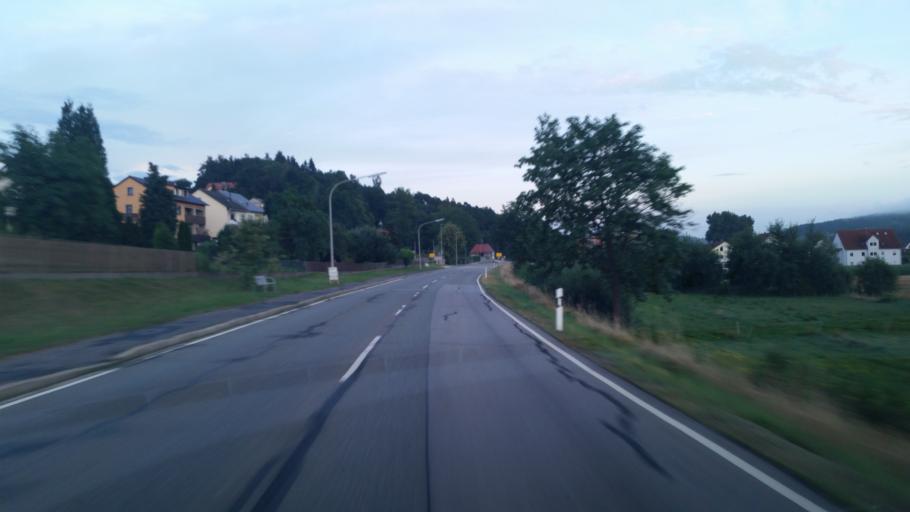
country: DE
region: Bavaria
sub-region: Upper Palatinate
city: Wernberg-Koblitz
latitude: 49.5446
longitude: 12.1558
